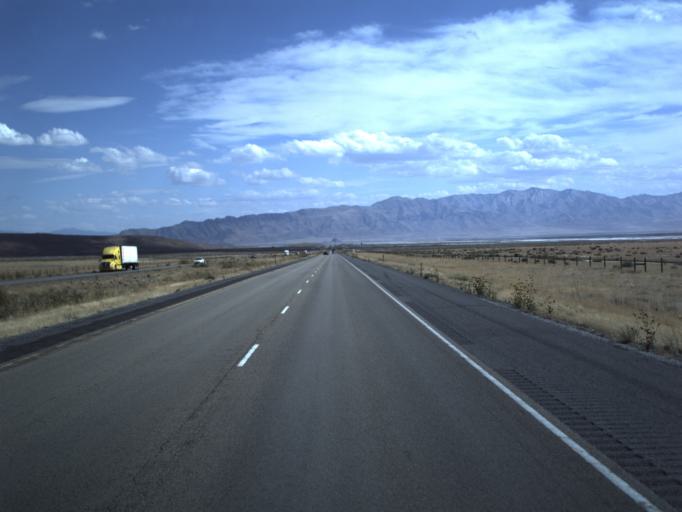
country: US
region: Utah
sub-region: Tooele County
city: Grantsville
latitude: 40.7952
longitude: -112.8409
